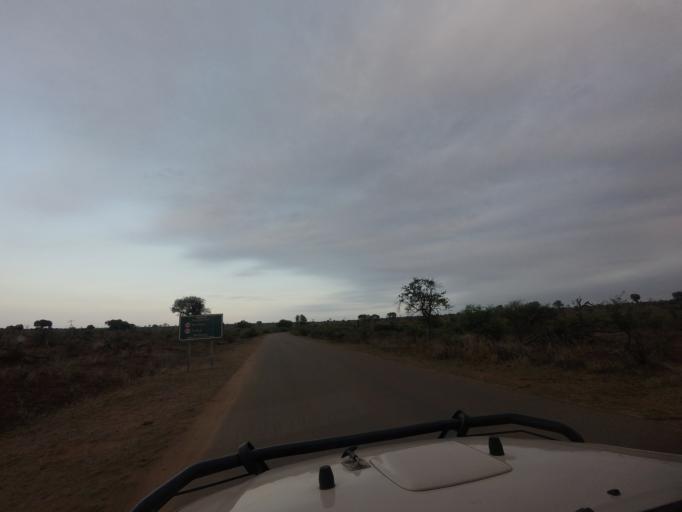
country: ZA
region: Mpumalanga
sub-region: Ehlanzeni District
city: Komatipoort
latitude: -25.3577
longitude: 31.8921
